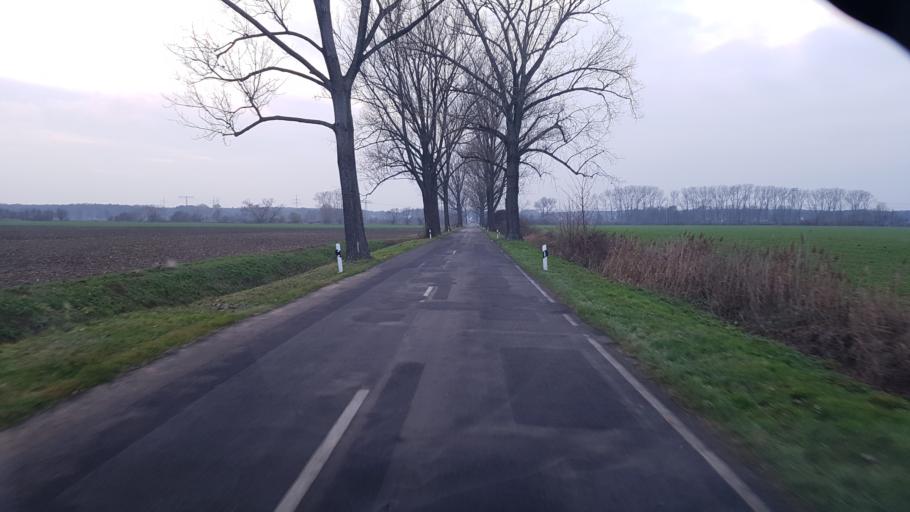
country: DE
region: Brandenburg
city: Ziltendorf
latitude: 52.2133
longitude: 14.6432
